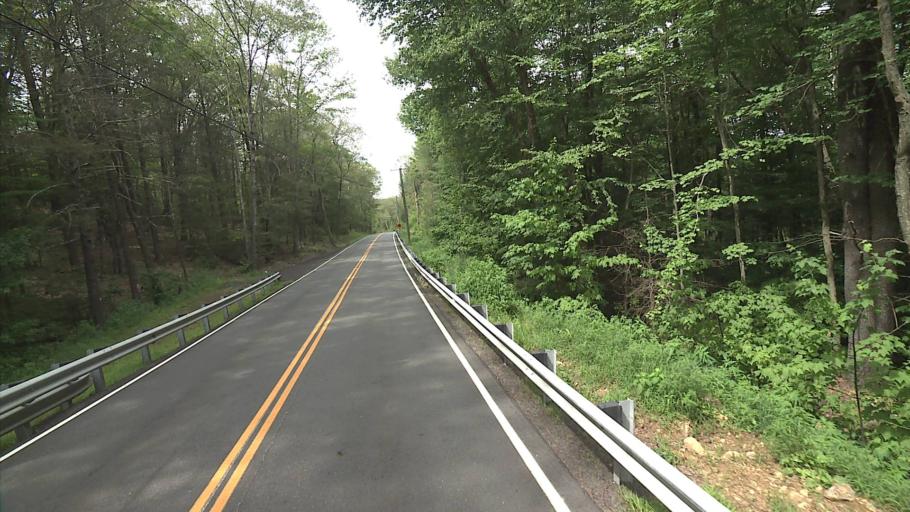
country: US
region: Massachusetts
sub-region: Hampden County
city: Holland
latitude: 41.9876
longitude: -72.1221
